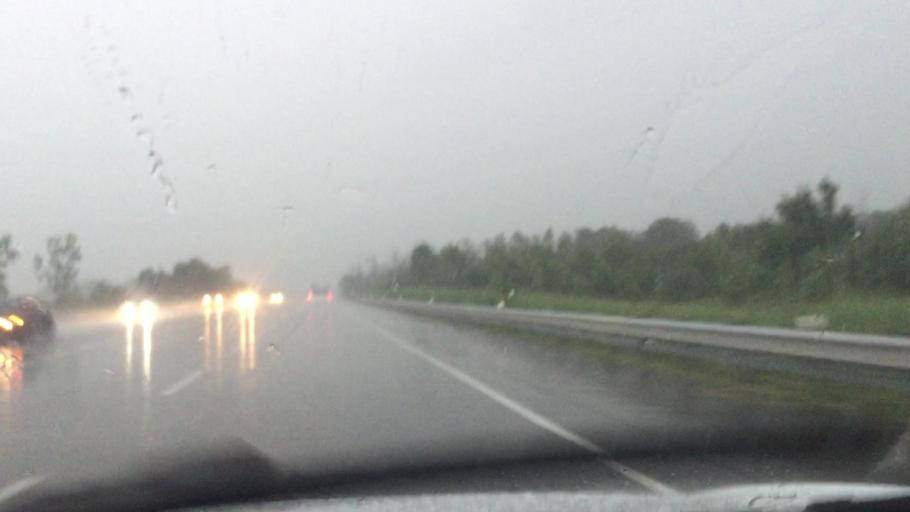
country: CA
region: Ontario
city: Pickering
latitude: 43.8581
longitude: -79.1596
